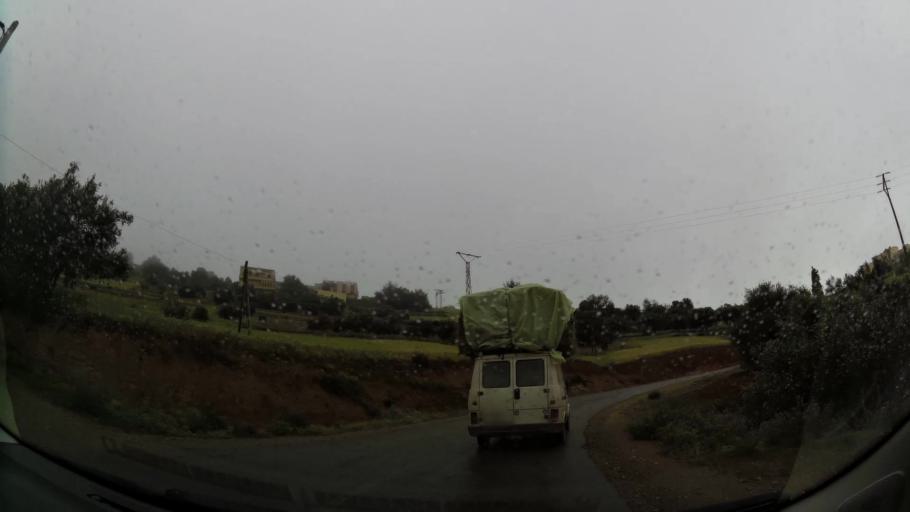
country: MA
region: Oriental
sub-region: Nador
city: Boudinar
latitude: 35.0914
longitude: -3.5265
